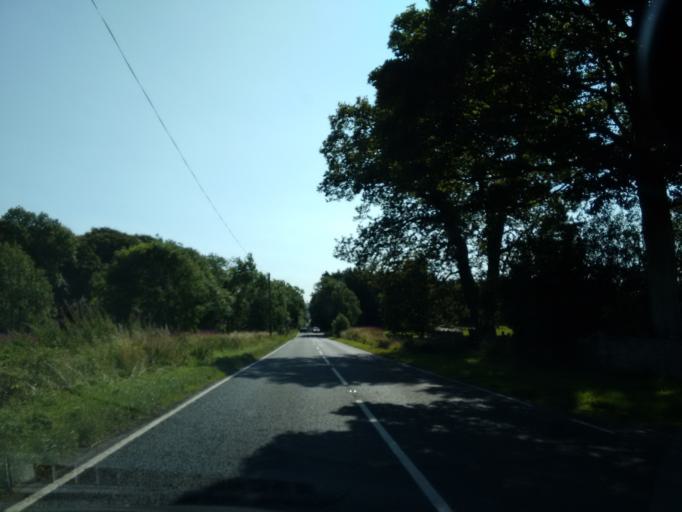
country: GB
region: England
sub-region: Northumberland
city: Corbridge
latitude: 55.0034
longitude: -2.0214
